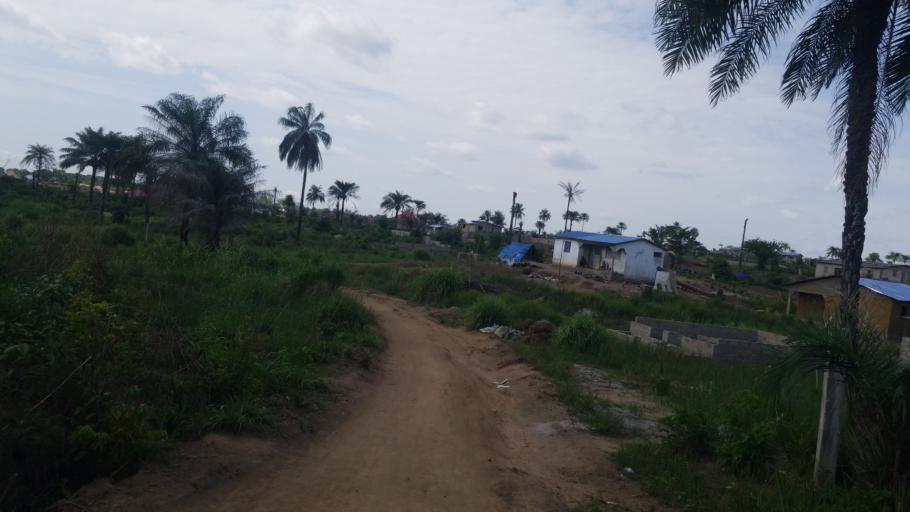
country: SL
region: Western Area
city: Waterloo
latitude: 8.3246
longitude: -13.0252
